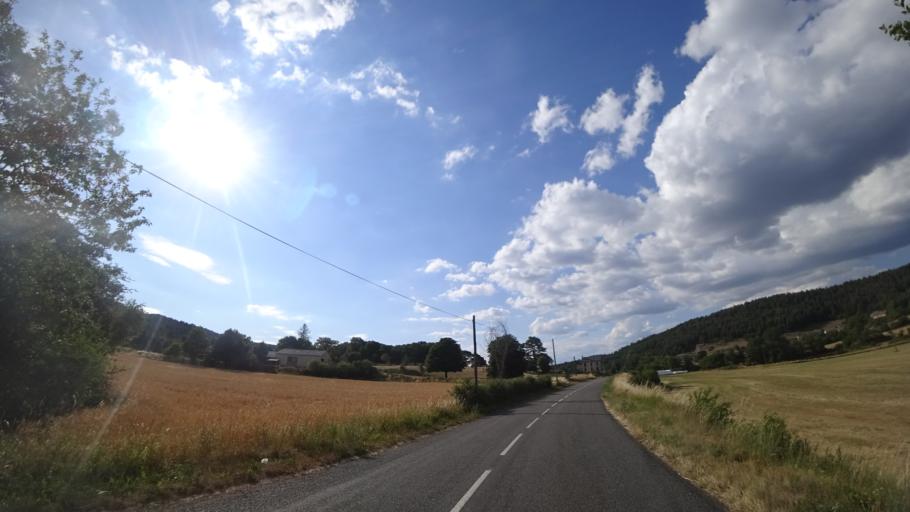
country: FR
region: Languedoc-Roussillon
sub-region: Departement de la Lozere
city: Chanac
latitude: 44.3861
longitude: 3.3050
